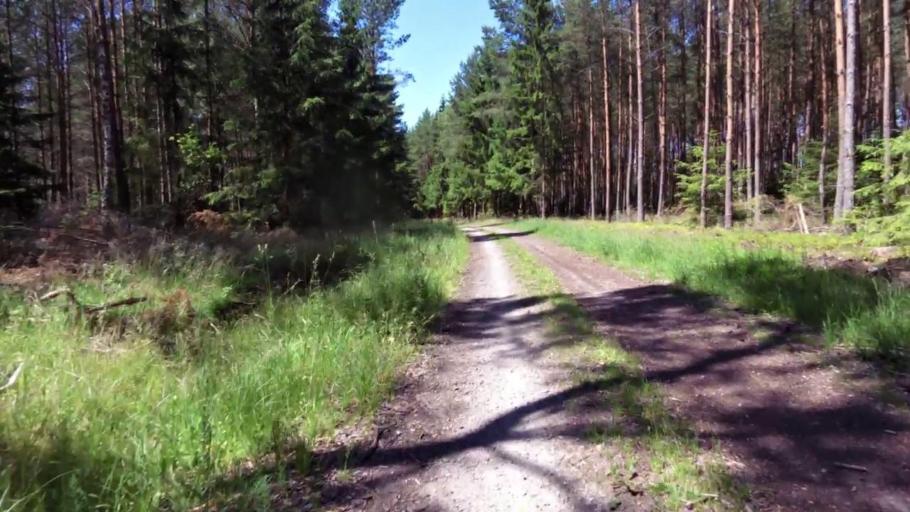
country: PL
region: West Pomeranian Voivodeship
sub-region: Powiat bialogardzki
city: Bialogard
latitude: 53.9531
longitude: 16.1056
